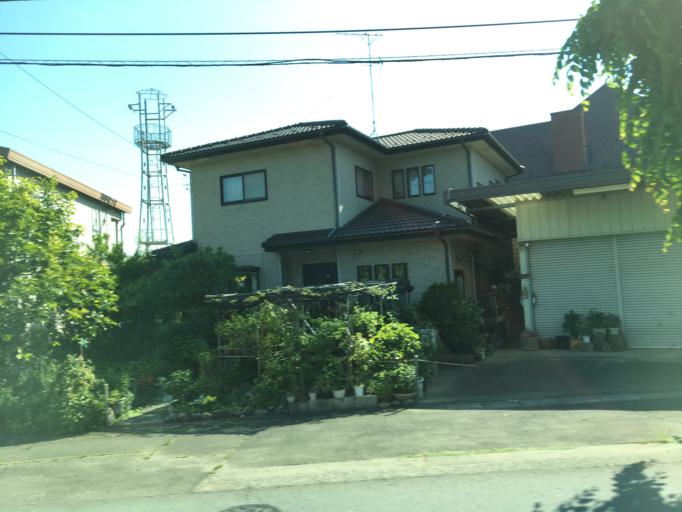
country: JP
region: Saitama
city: Morohongo
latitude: 35.9709
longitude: 139.3404
